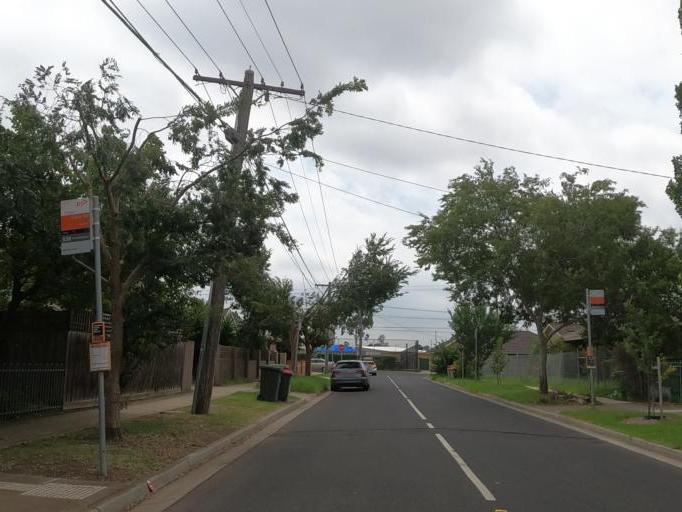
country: AU
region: Victoria
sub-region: Hume
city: Broadmeadows
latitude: -37.6863
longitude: 144.9231
